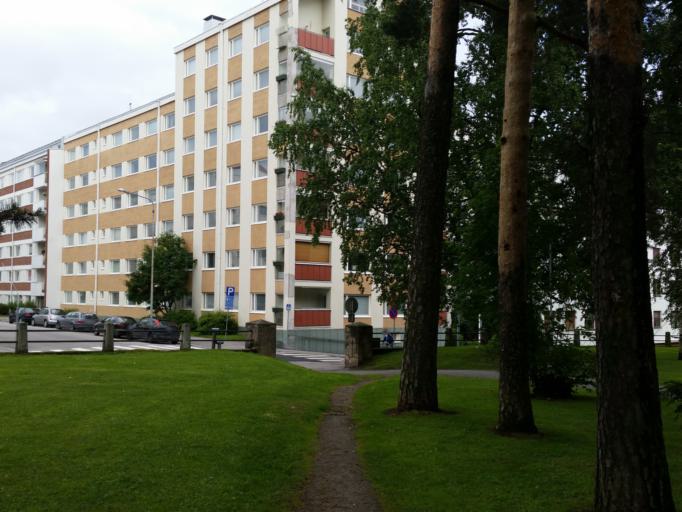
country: FI
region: Northern Savo
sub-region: Kuopio
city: Kuopio
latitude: 62.8944
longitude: 27.6735
